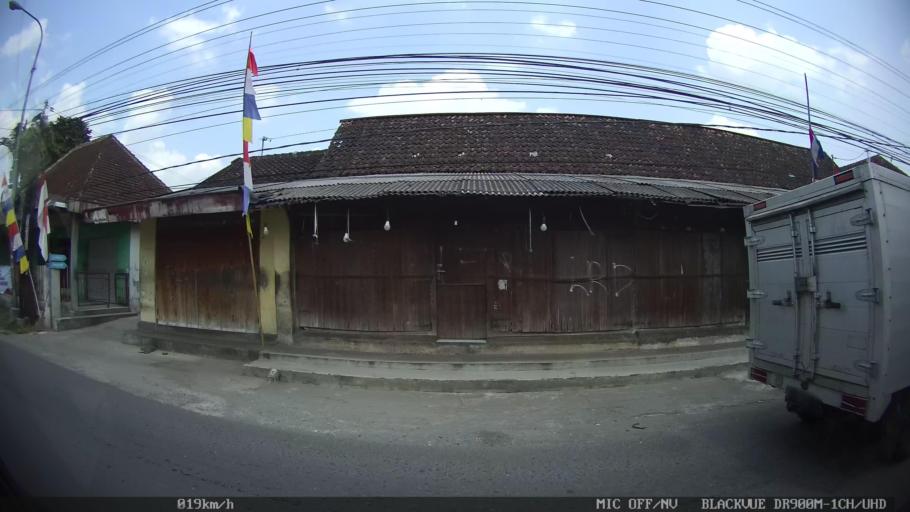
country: ID
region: Daerah Istimewa Yogyakarta
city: Yogyakarta
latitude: -7.8283
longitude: 110.4056
